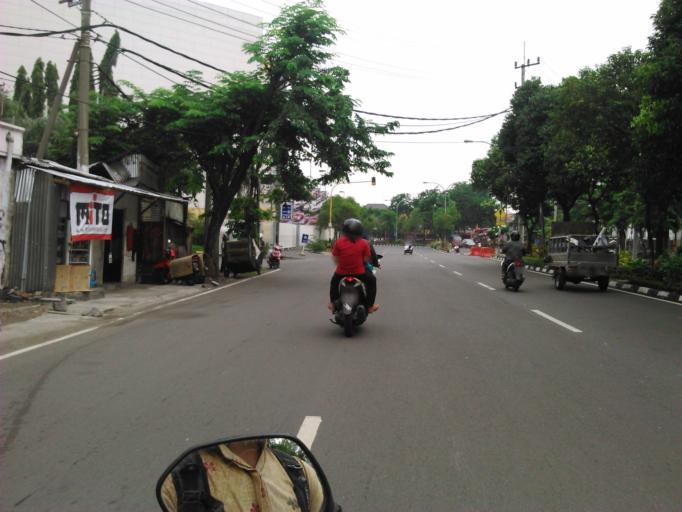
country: ID
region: East Java
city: Pacarkeling
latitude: -7.2636
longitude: 112.7518
